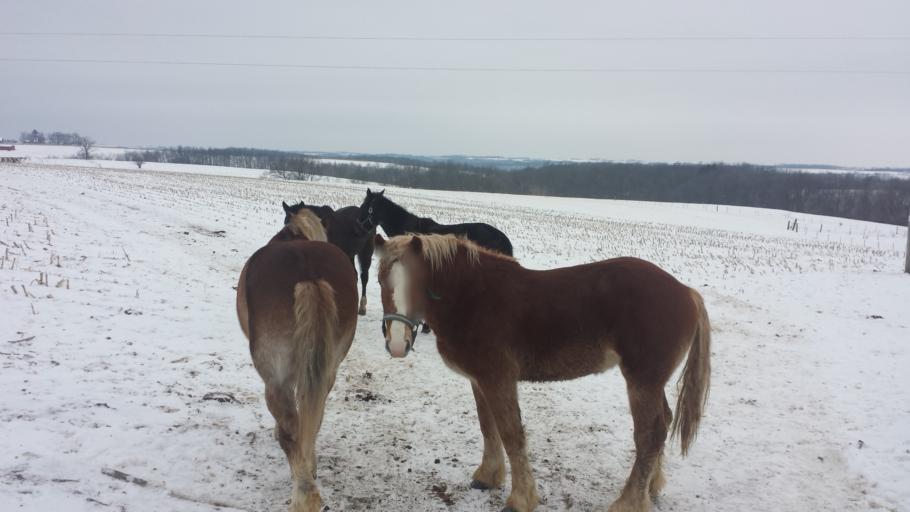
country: US
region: Wisconsin
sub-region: Monroe County
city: Cashton
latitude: 43.7708
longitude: -90.6588
